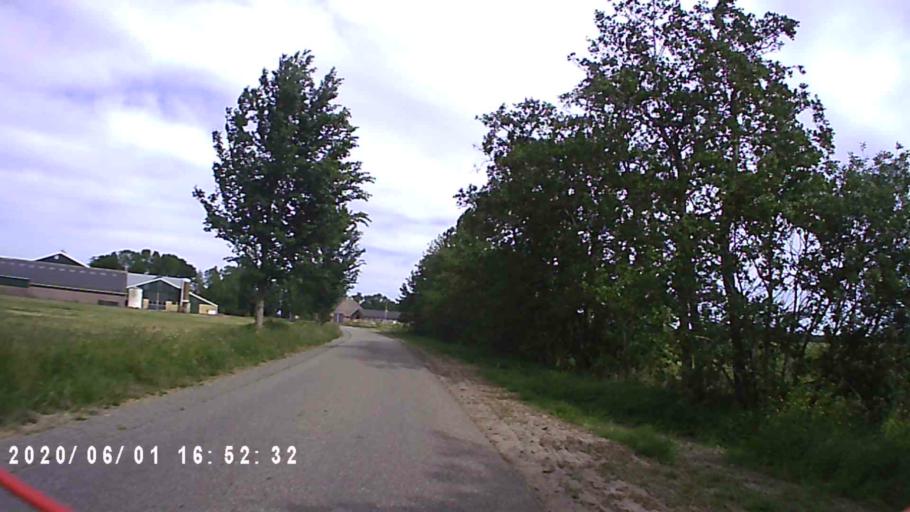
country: NL
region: Friesland
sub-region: Gemeente Tytsjerksteradiel
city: Tytsjerk
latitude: 53.1894
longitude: 5.9166
